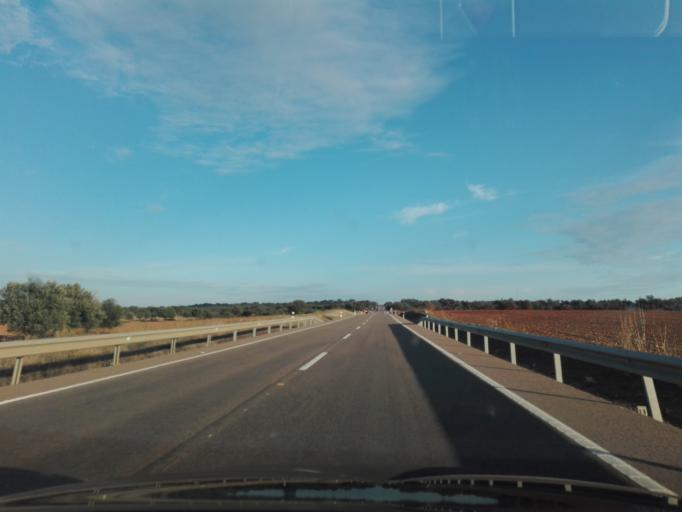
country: ES
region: Extremadura
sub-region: Provincia de Badajoz
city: Usagre
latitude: 38.3706
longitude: -6.2475
